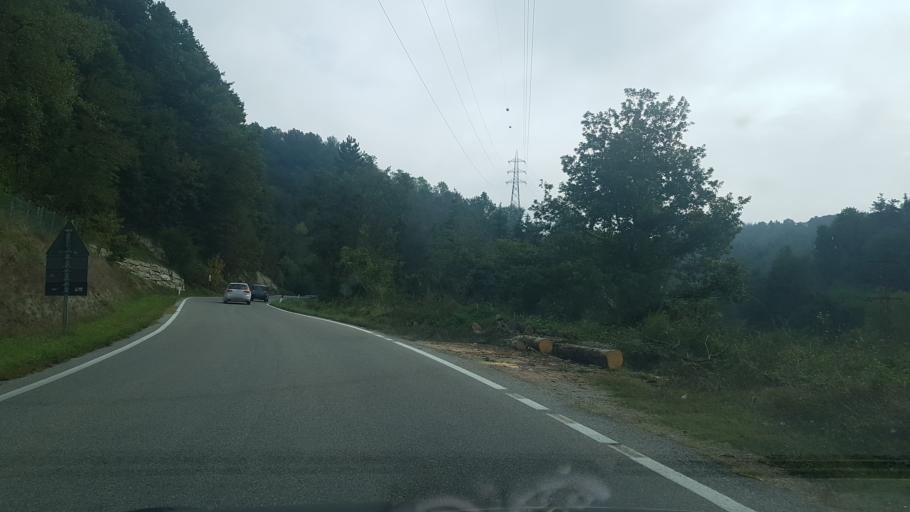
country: IT
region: Piedmont
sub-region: Provincia di Cuneo
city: Sale delle Langhe
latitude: 44.4011
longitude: 8.1043
